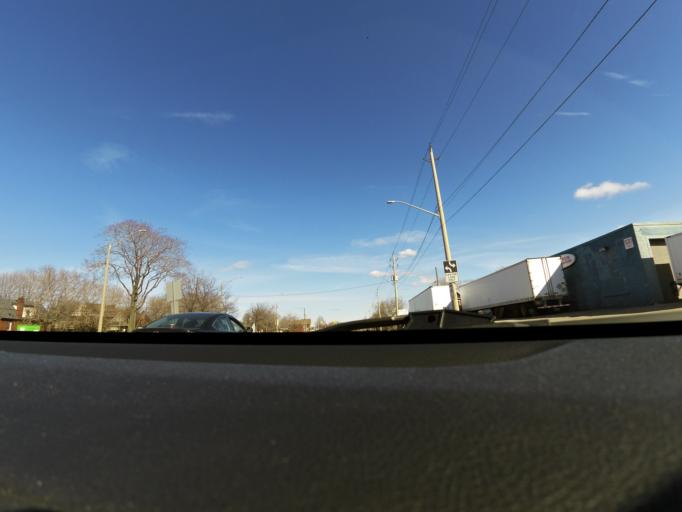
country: CA
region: Ontario
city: Hamilton
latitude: 43.2678
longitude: -79.8420
